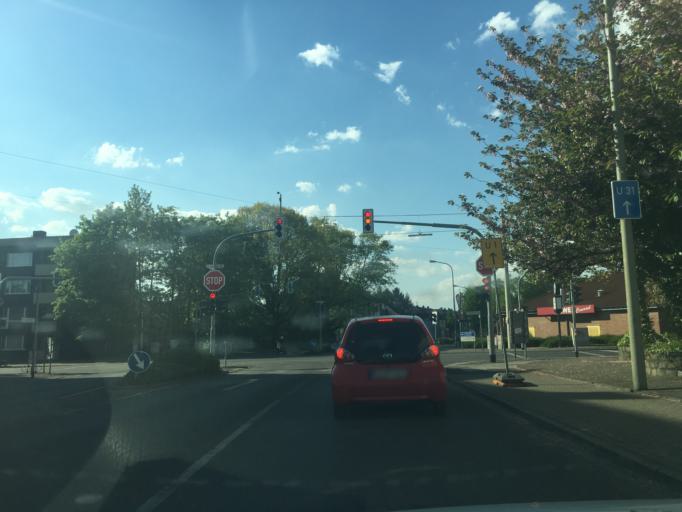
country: DE
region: North Rhine-Westphalia
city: Haan
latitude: 51.1864
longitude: 6.9905
